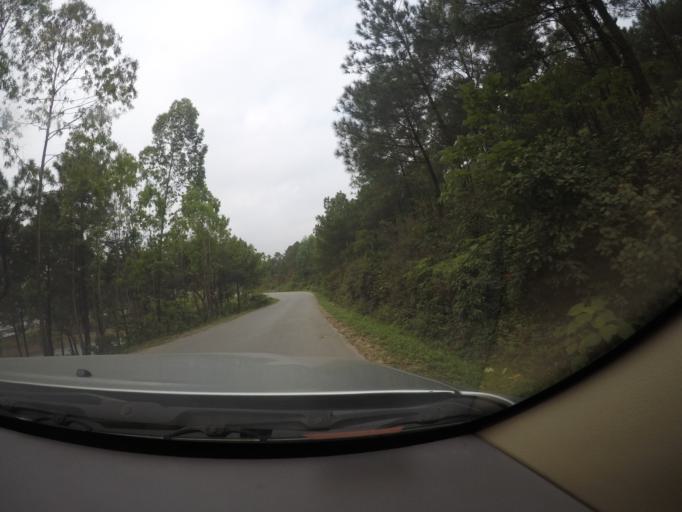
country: VN
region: Quang Binh
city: Ba Don
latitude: 17.6861
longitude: 106.4268
